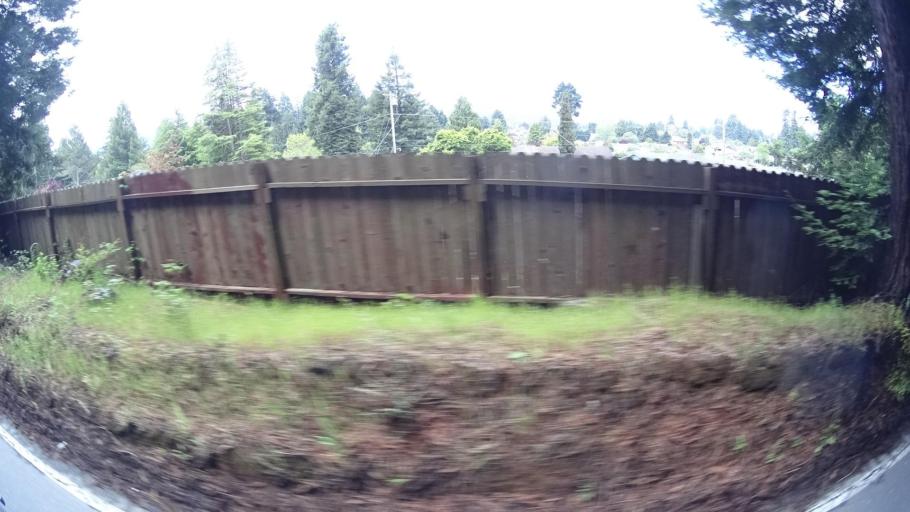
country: US
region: California
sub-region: Humboldt County
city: Blue Lake
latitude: 40.8808
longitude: -123.9785
